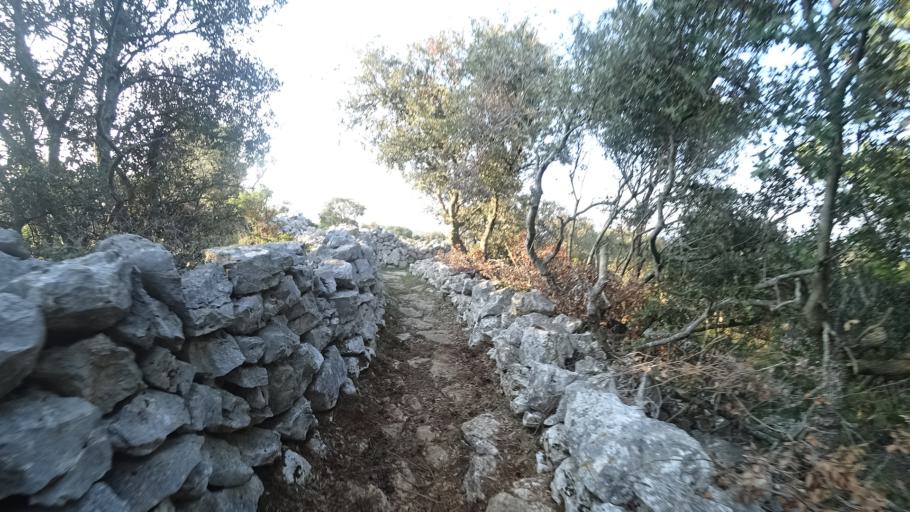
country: HR
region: Primorsko-Goranska
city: Mali Losinj
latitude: 44.5242
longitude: 14.4758
